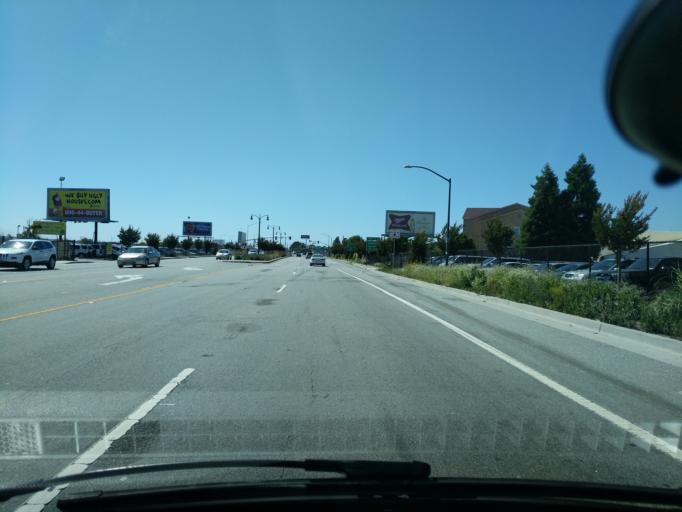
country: US
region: California
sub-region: Alameda County
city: San Leandro
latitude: 37.7247
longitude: -122.1976
